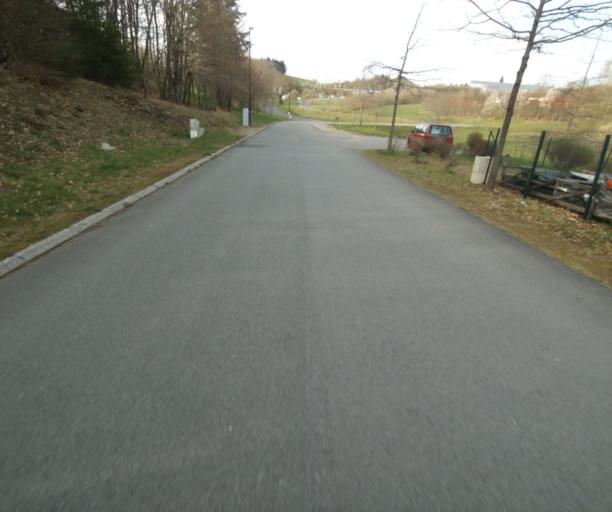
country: FR
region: Limousin
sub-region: Departement de la Correze
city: Naves
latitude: 45.3228
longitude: 1.7656
